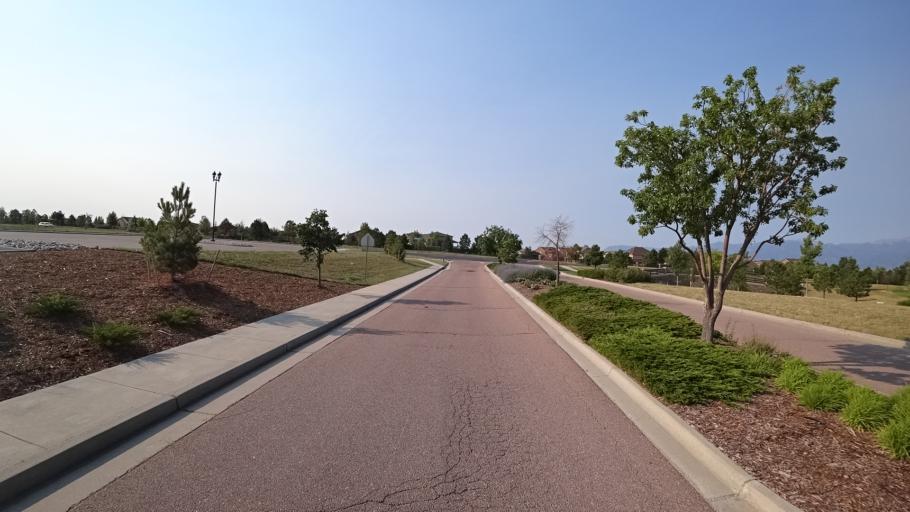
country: US
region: Colorado
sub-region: El Paso County
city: Black Forest
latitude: 38.9719
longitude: -104.7353
